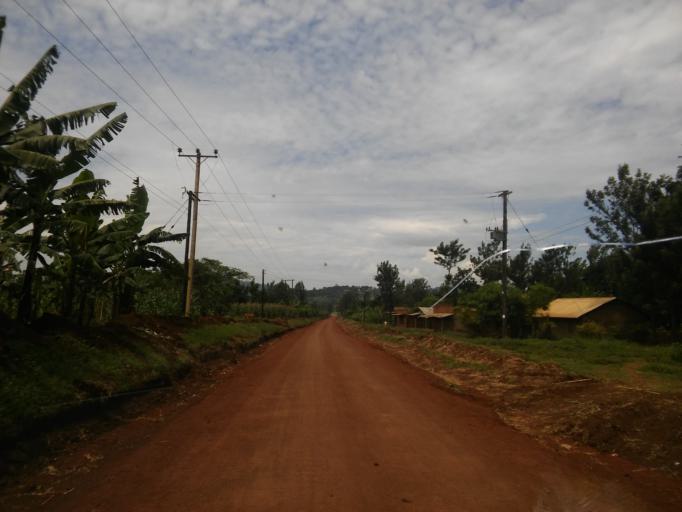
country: UG
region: Eastern Region
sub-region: Manafwa District
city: Manafwa
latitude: 0.8487
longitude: 34.2704
